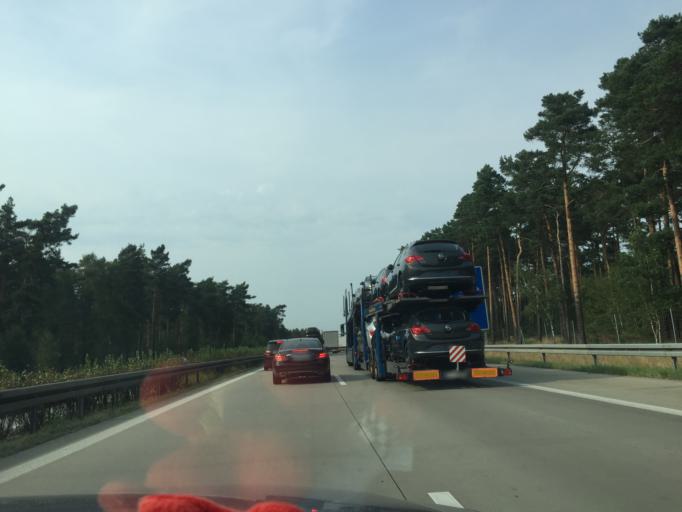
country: DE
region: Brandenburg
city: Halbe
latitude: 52.0567
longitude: 13.6543
